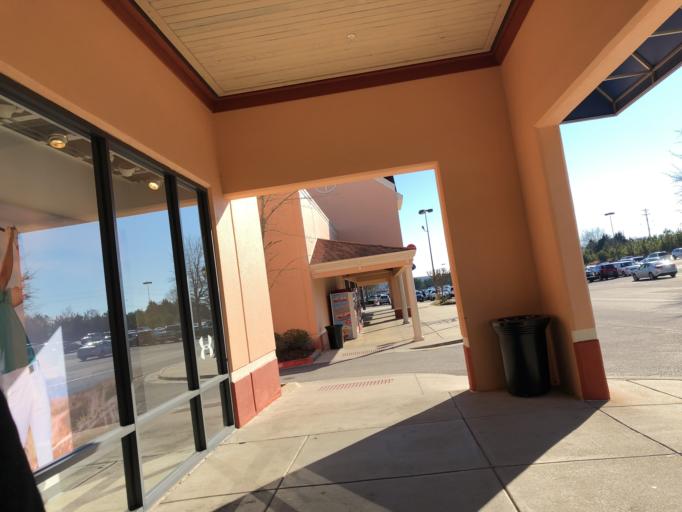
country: US
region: Georgia
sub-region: Dawson County
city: Dawsonville
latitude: 34.3591
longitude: -84.0488
